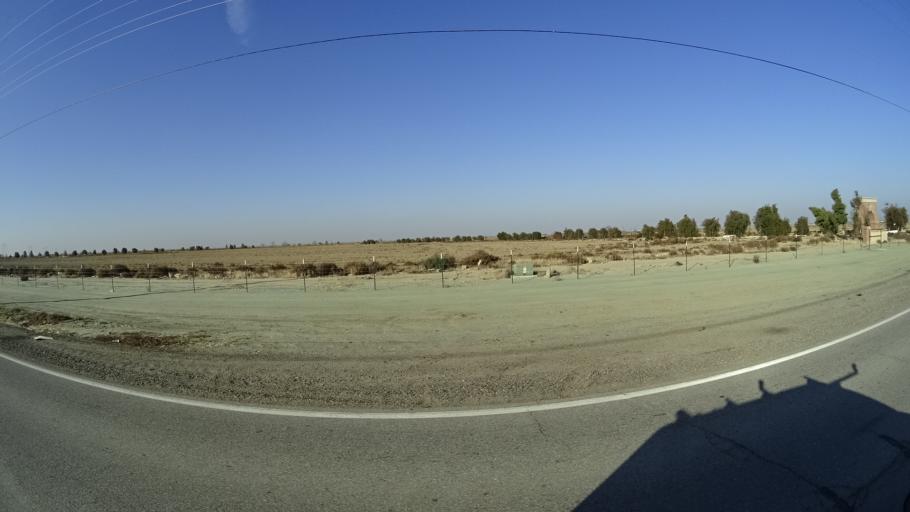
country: US
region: California
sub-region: Kern County
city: Rosedale
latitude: 35.2962
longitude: -119.1645
